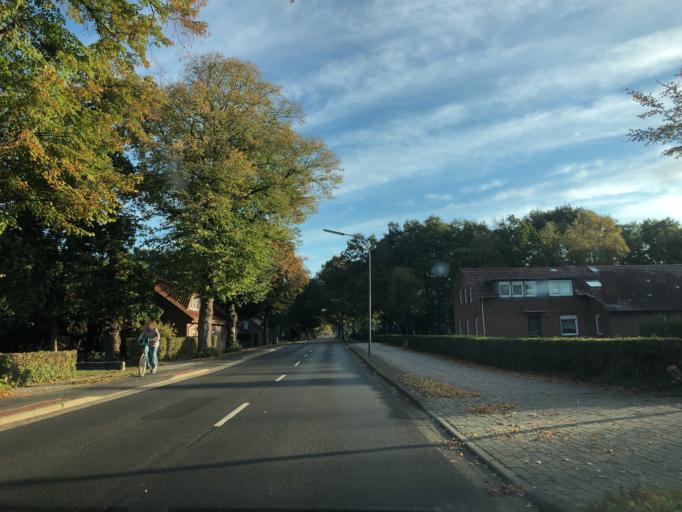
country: DE
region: Lower Saxony
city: Lehe
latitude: 53.0559
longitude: 7.3443
